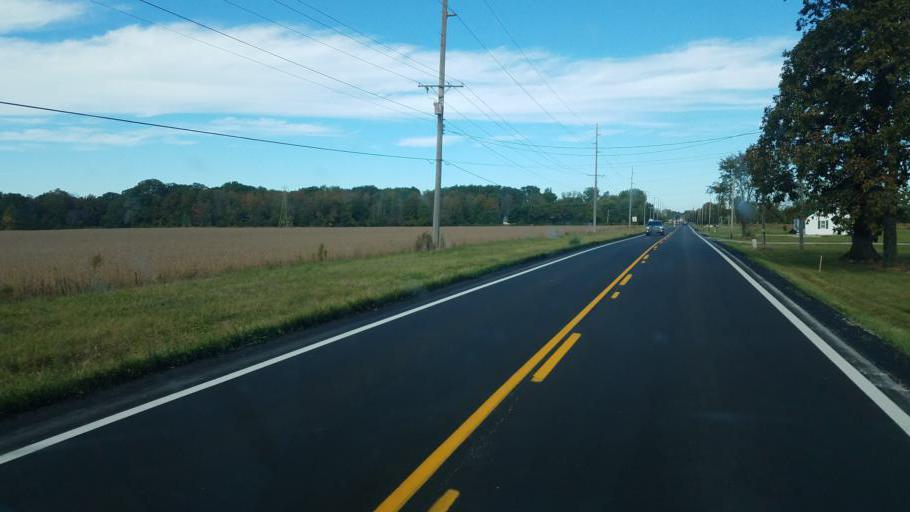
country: US
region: Ohio
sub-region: Erie County
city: Huron
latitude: 41.3544
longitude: -82.4940
